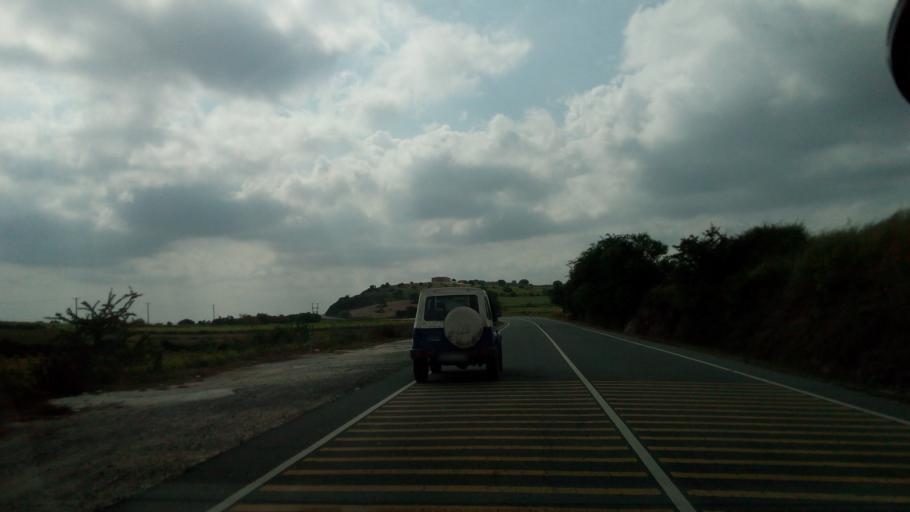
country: CY
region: Pafos
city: Pegeia
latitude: 34.9091
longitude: 32.4368
